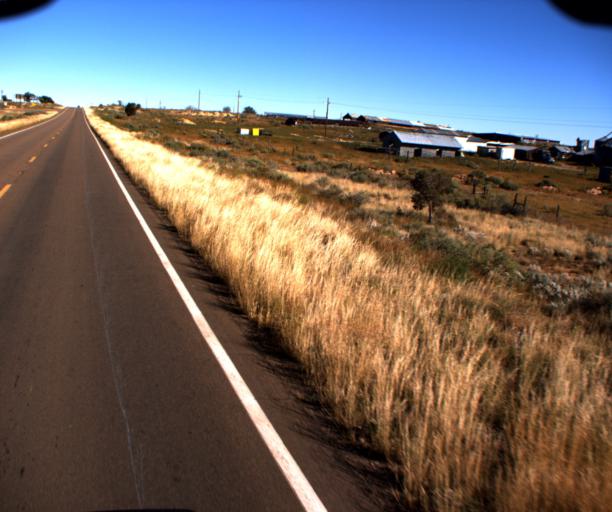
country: US
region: Arizona
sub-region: Navajo County
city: Snowflake
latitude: 34.5579
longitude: -110.0811
